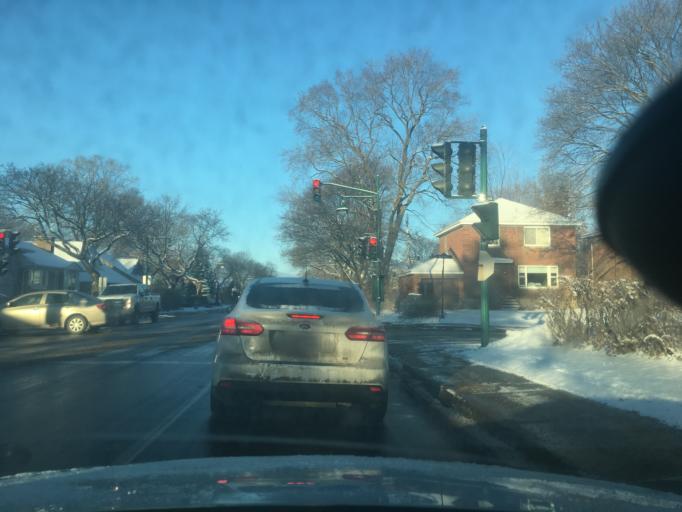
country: CA
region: Quebec
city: Saint-Laurent
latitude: 45.5060
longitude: -73.6563
